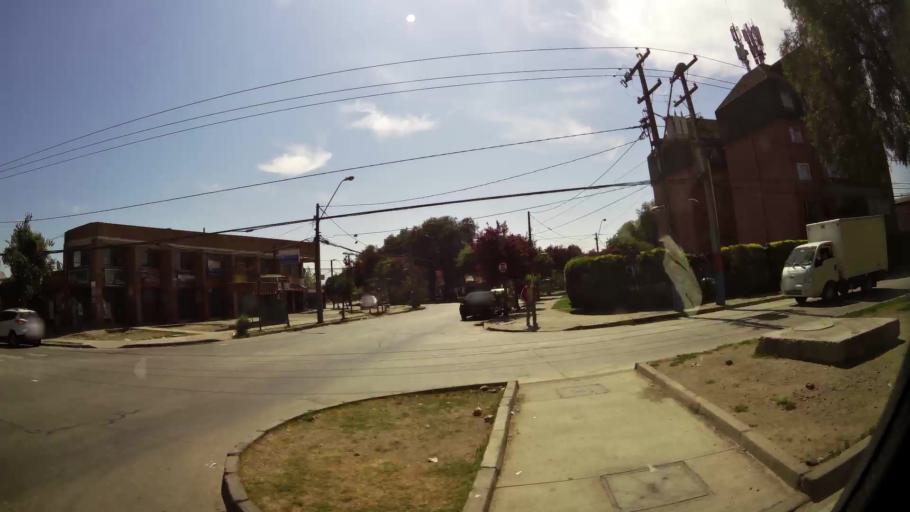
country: CL
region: Santiago Metropolitan
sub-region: Provincia de Santiago
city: Lo Prado
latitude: -33.4908
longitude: -70.7382
